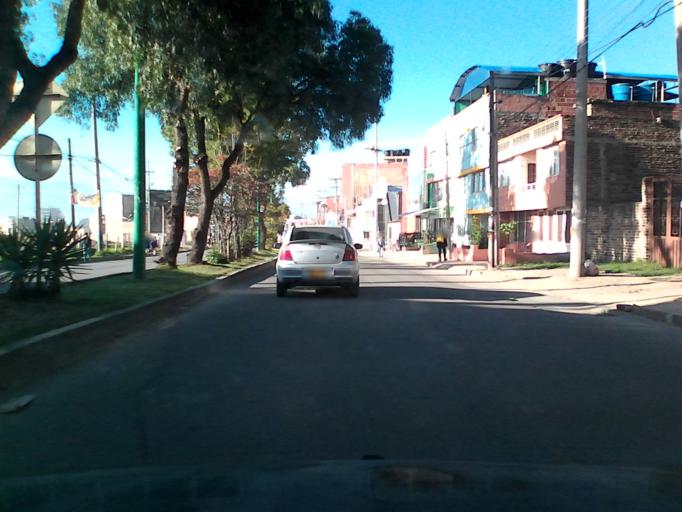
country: CO
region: Boyaca
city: Duitama
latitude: 5.8219
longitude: -73.0279
